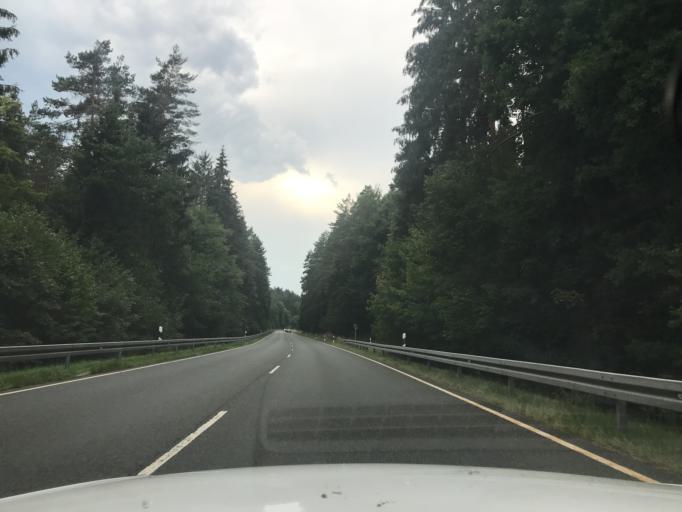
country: DE
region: Bavaria
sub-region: Upper Franconia
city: Pegnitz
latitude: 49.7178
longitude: 11.5394
